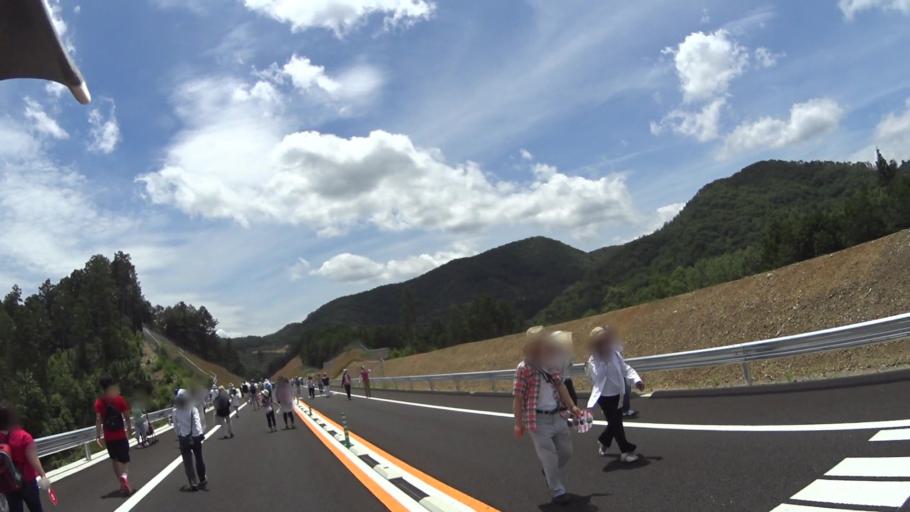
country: JP
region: Kyoto
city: Ayabe
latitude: 35.1648
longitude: 135.3859
